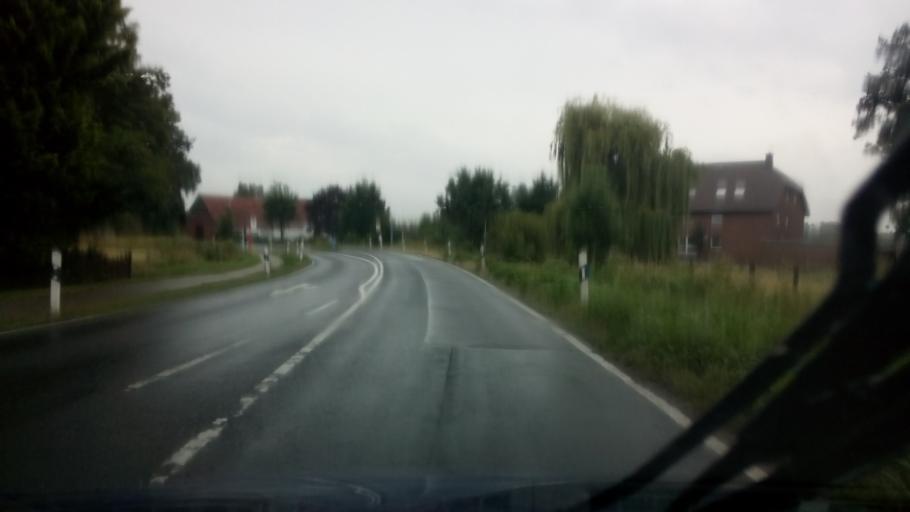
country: DE
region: Lower Saxony
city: Melle
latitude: 52.2132
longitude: 8.3194
